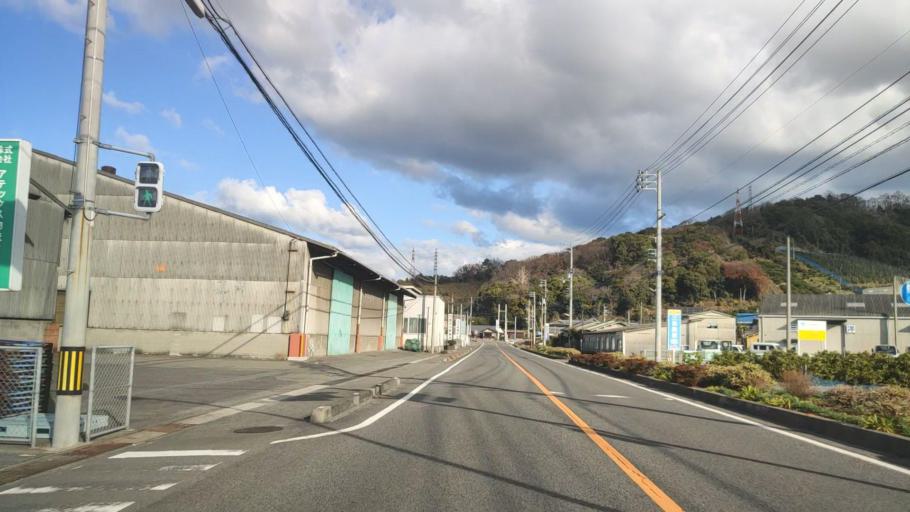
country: JP
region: Ehime
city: Masaki-cho
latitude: 33.8383
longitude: 132.7092
